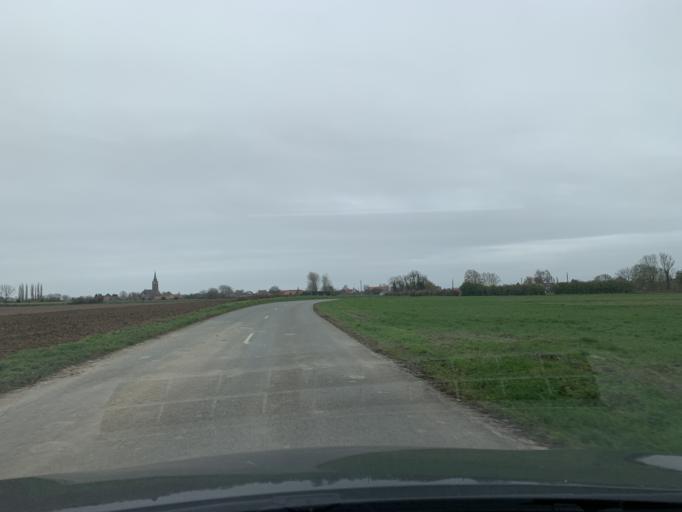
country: FR
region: Nord-Pas-de-Calais
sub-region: Departement du Nord
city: Aubigny-au-Bac
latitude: 50.2348
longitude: 3.1564
